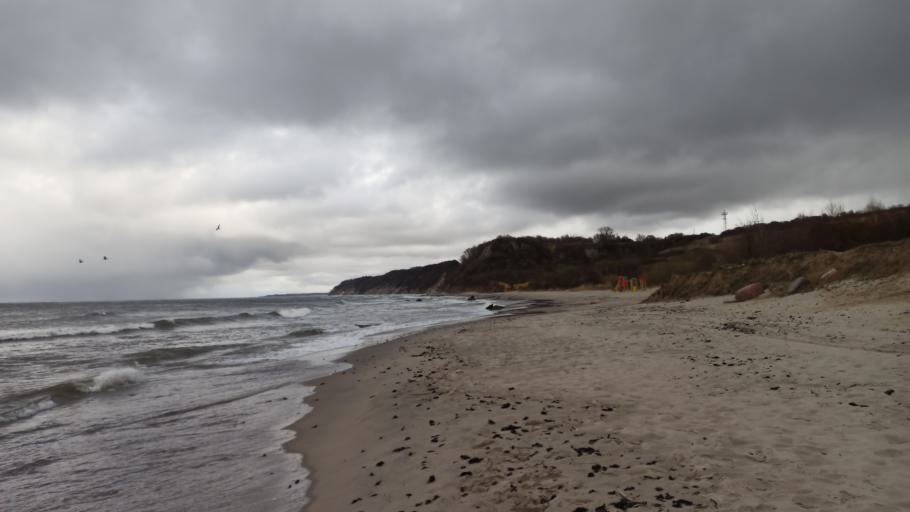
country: RU
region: Kaliningrad
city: Donskoye
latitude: 54.9480
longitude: 20.0195
